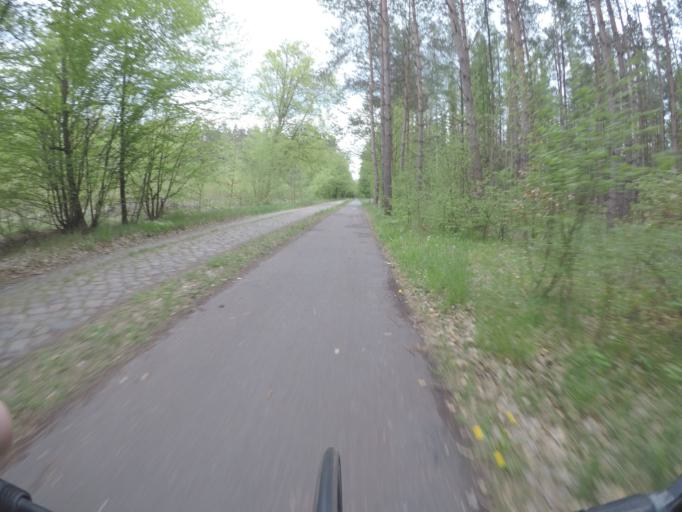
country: DE
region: Brandenburg
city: Marienwerder
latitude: 52.8317
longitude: 13.6284
